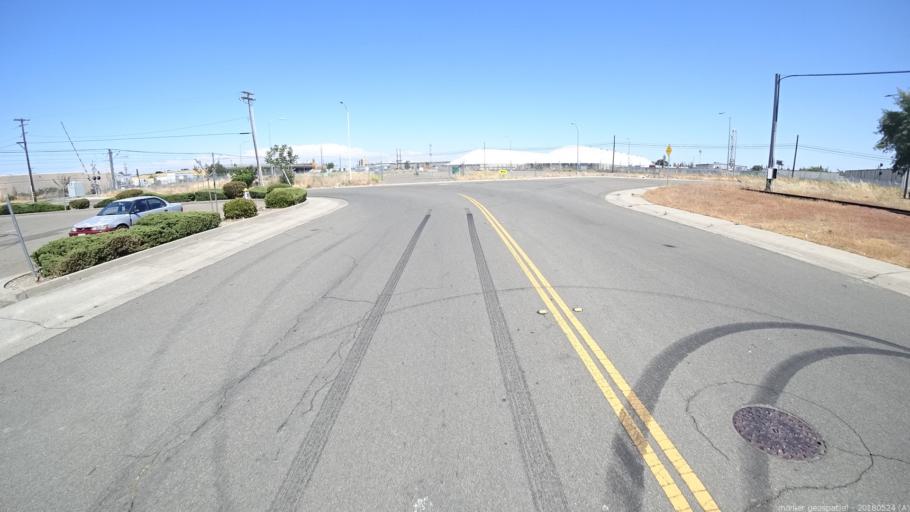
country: US
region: California
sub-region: Sacramento County
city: Sacramento
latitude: 38.6046
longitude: -121.4443
